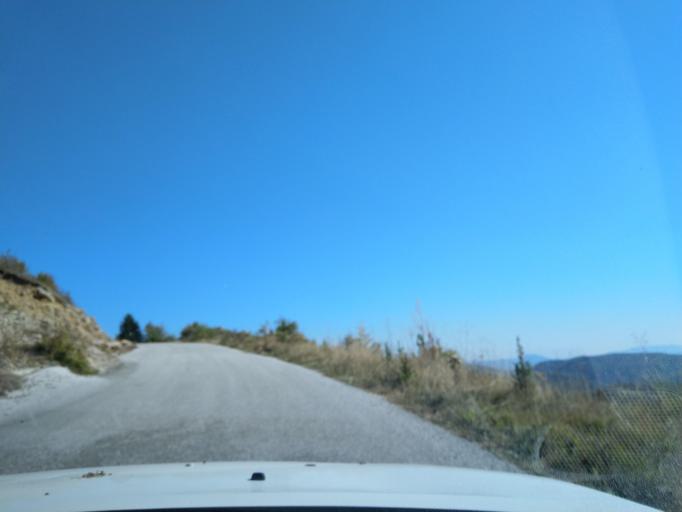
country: RS
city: Sokolovica
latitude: 43.2500
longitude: 20.3275
